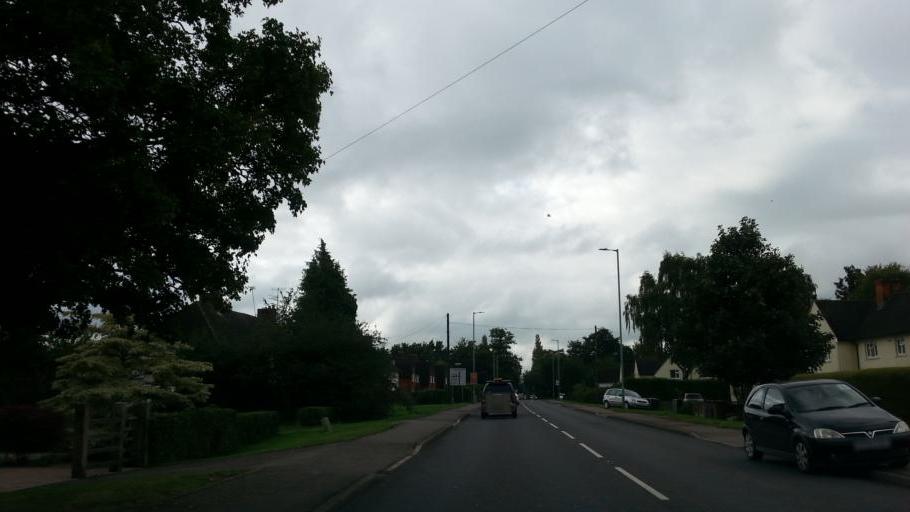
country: GB
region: England
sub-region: Hertfordshire
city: Hitchin
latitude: 51.9692
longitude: -0.2875
